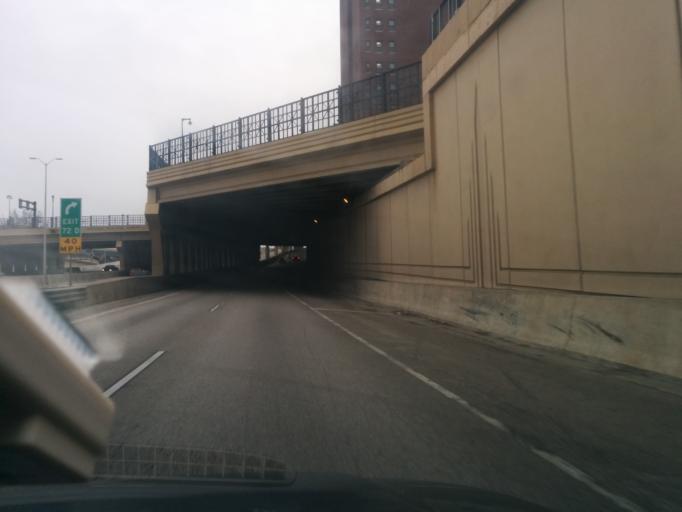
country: US
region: Wisconsin
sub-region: Milwaukee County
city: Milwaukee
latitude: 43.0398
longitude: -87.9251
